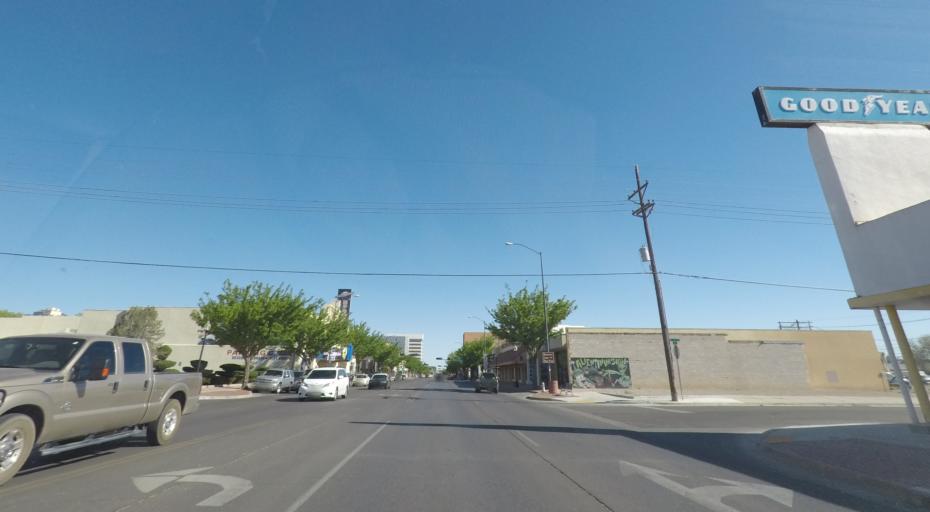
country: US
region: New Mexico
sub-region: Chaves County
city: Roswell
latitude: 33.3929
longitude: -104.5228
